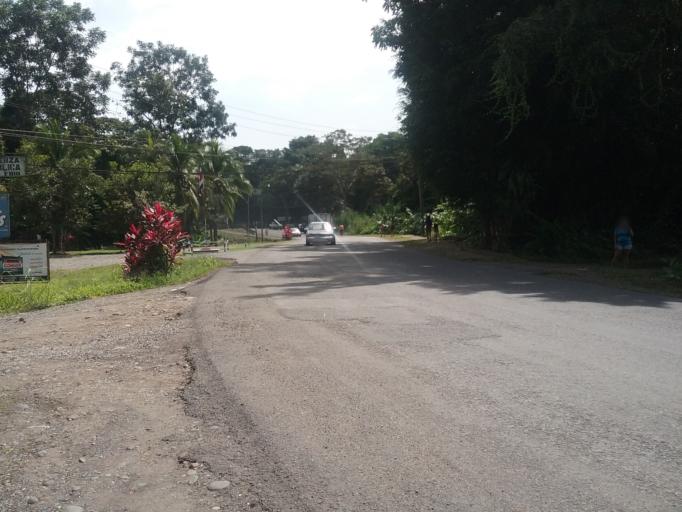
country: CR
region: Limon
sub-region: Canton de Pococi
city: Guapiles
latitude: 10.3204
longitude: -83.8924
